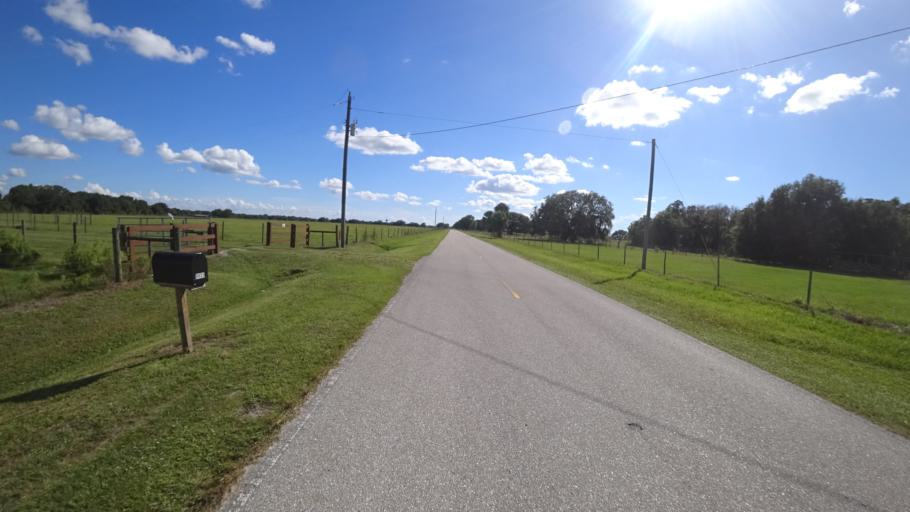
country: US
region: Florida
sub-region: Sarasota County
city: North Port
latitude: 27.2042
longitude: -82.1222
